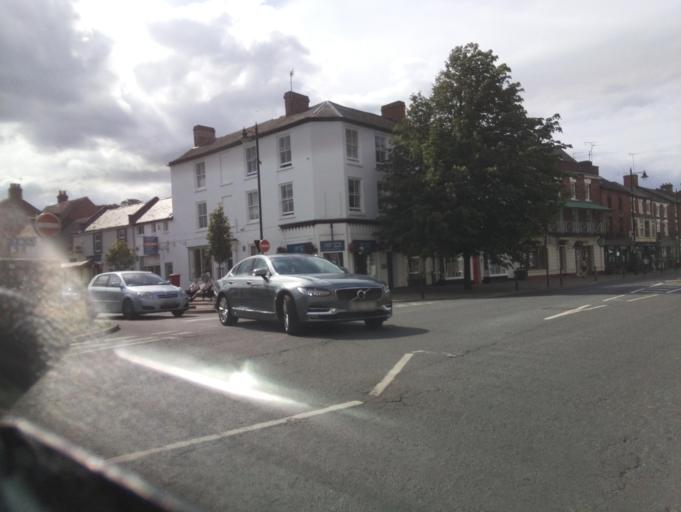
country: GB
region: England
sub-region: Worcestershire
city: Pershore
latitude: 52.1100
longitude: -2.0746
